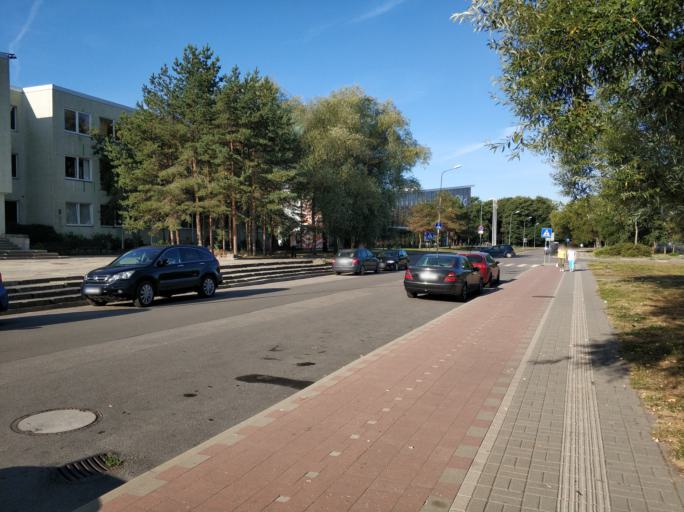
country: LV
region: Liepaja
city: Liepaja
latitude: 56.4912
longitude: 21.0024
